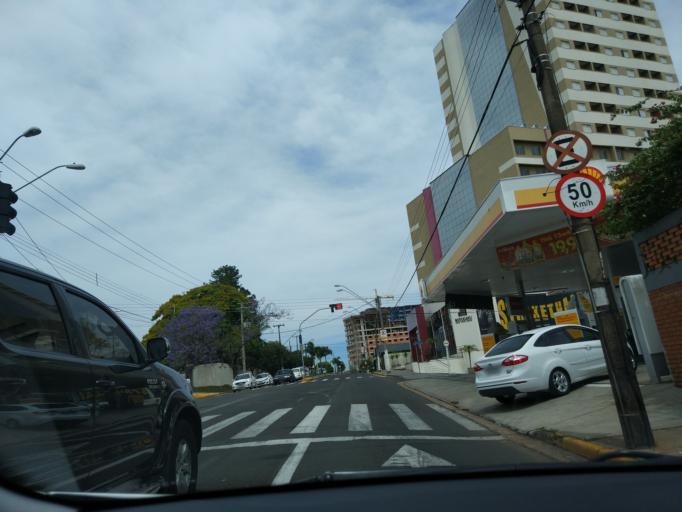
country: BR
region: Sao Paulo
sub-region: Botucatu
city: Botucatu
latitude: -22.8855
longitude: -48.4536
